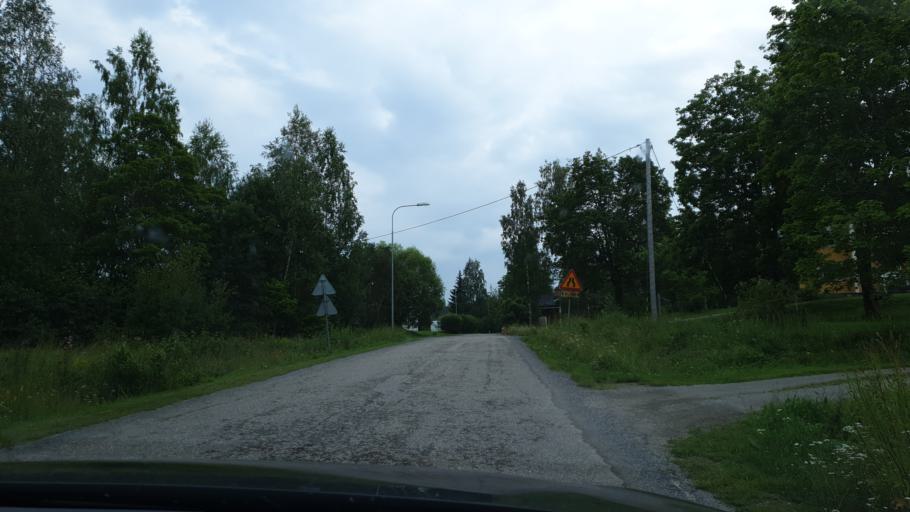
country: SE
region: Gaevleborg
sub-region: Hudiksvalls Kommun
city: Iggesund
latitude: 61.5436
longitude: 17.0040
